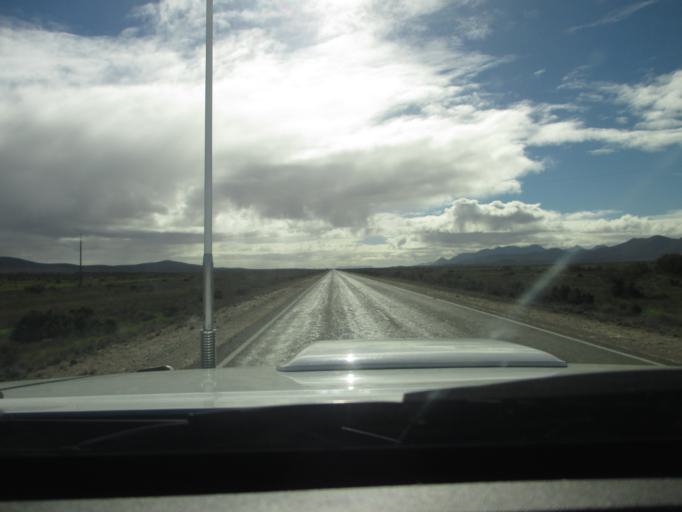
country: AU
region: South Australia
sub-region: Flinders Ranges
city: Quorn
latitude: -31.6799
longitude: 138.3664
